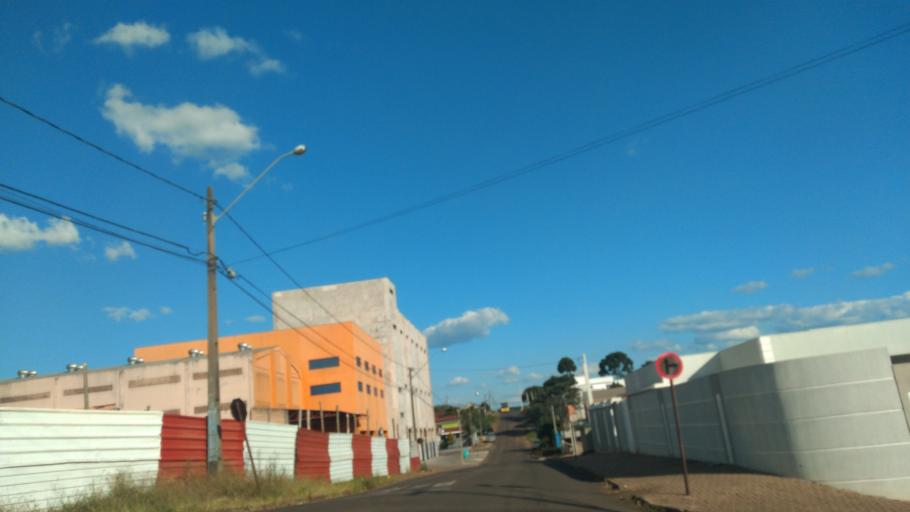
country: BR
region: Parana
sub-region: Guarapuava
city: Guarapuava
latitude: -25.3995
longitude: -51.4819
